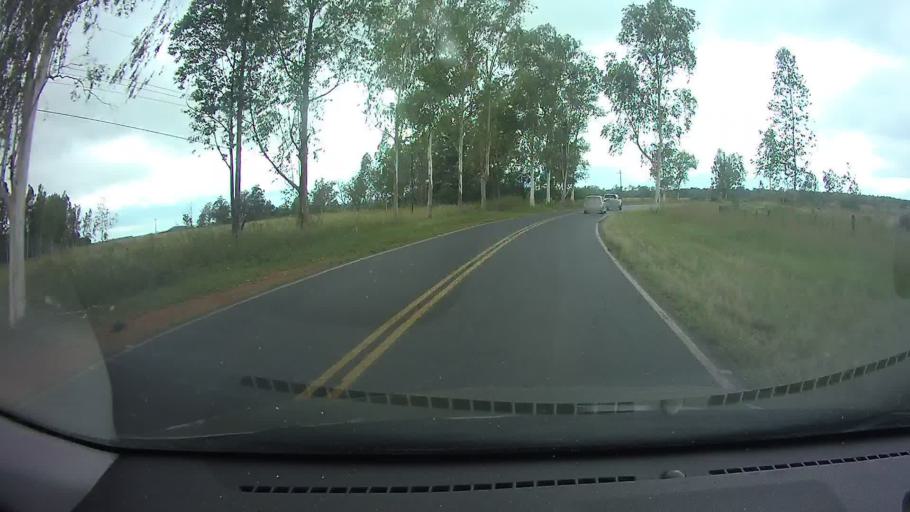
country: PY
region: Central
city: Nueva Italia
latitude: -25.5577
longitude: -57.5011
